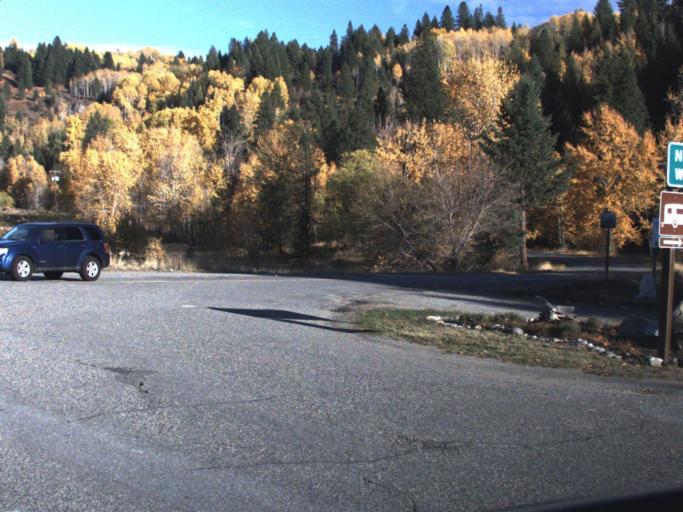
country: CA
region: British Columbia
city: Rossland
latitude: 48.9178
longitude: -117.7773
